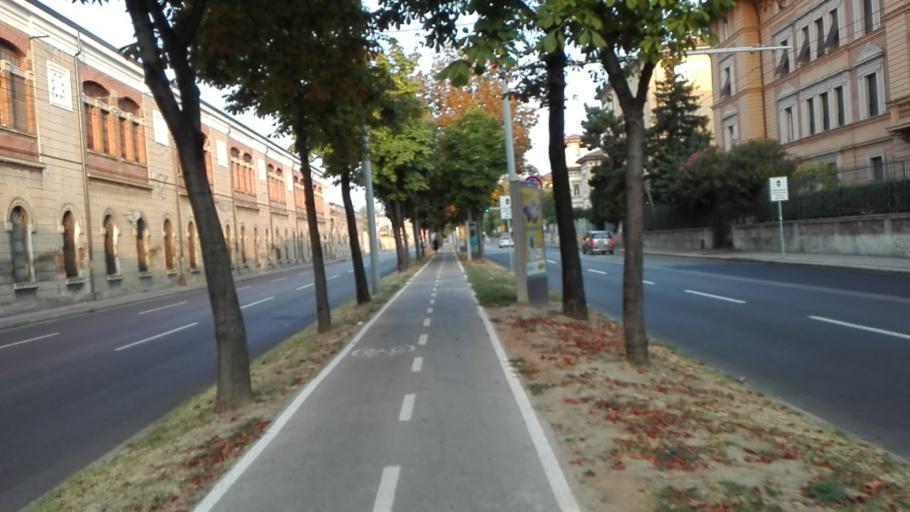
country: IT
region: Emilia-Romagna
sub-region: Provincia di Bologna
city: Bologna
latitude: 44.4857
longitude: 11.3459
